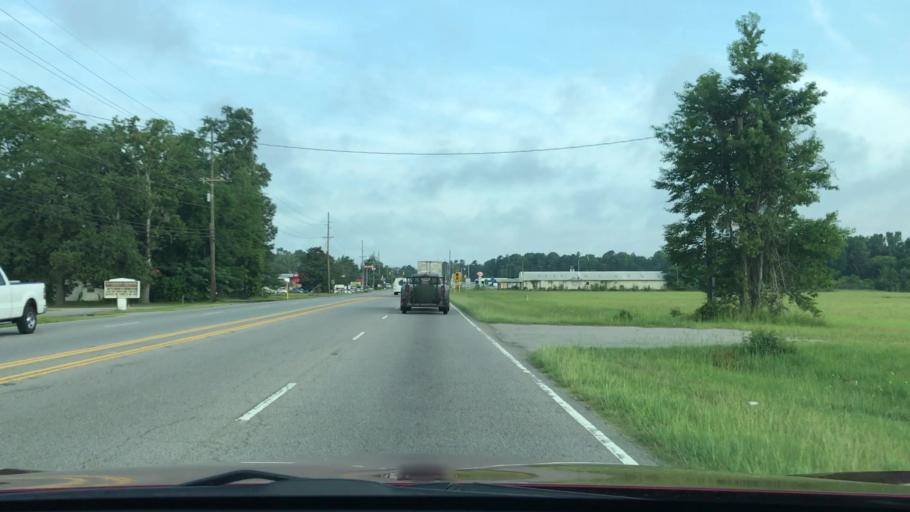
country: US
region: South Carolina
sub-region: Orangeburg County
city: Wilkinson Heights
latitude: 33.4839
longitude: -80.8284
